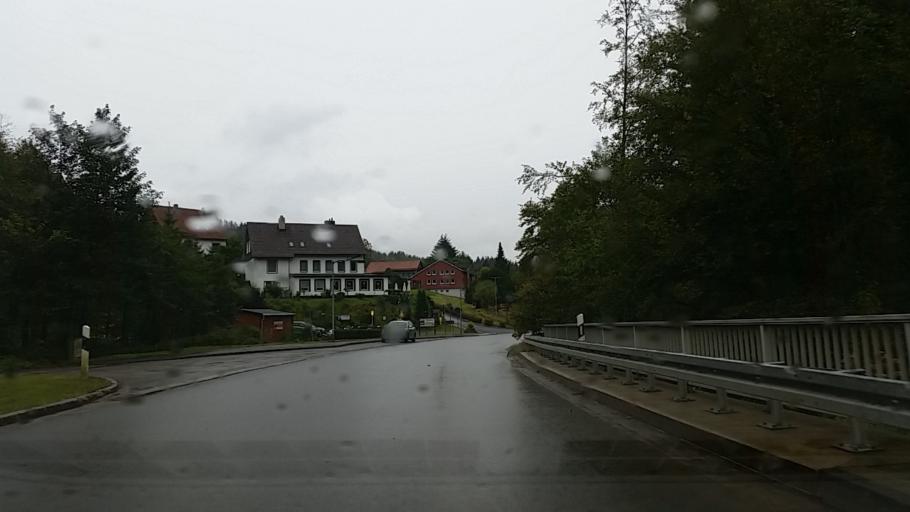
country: DE
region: Lower Saxony
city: Altenau
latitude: 51.7545
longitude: 10.3887
